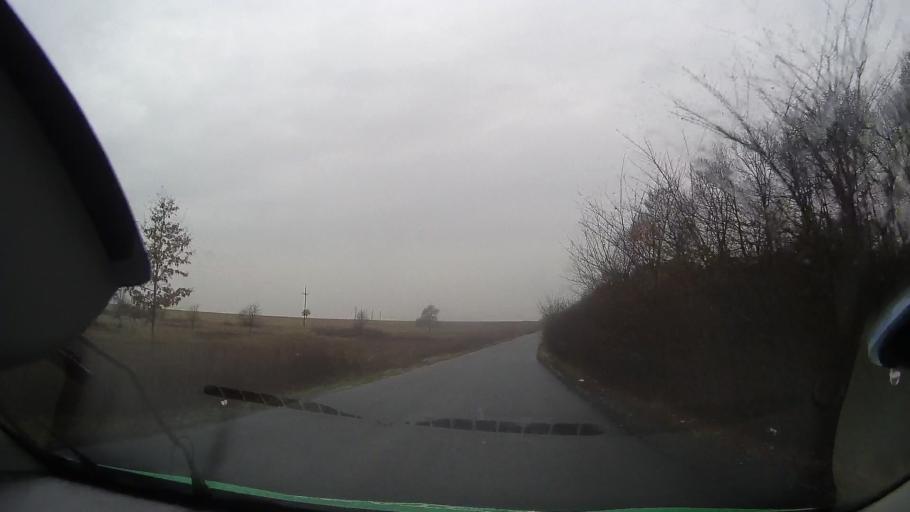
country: RO
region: Bihor
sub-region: Comuna Tinca
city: Gurbediu
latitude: 46.7750
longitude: 21.8822
